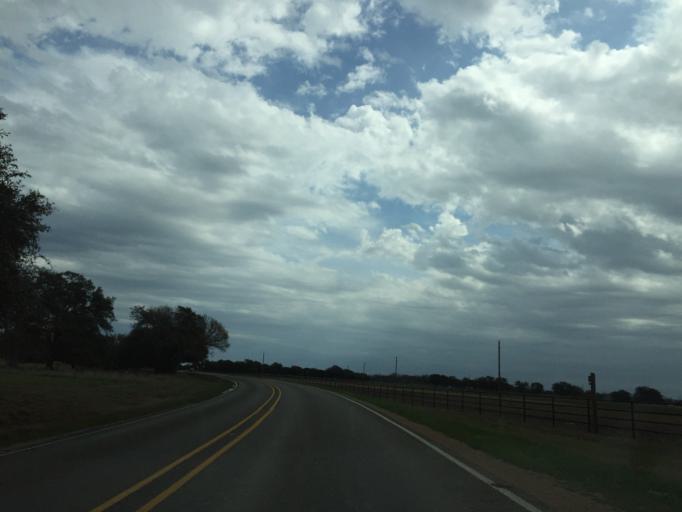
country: US
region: Texas
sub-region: Burnet County
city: Bertram
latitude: 30.6543
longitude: -98.0024
